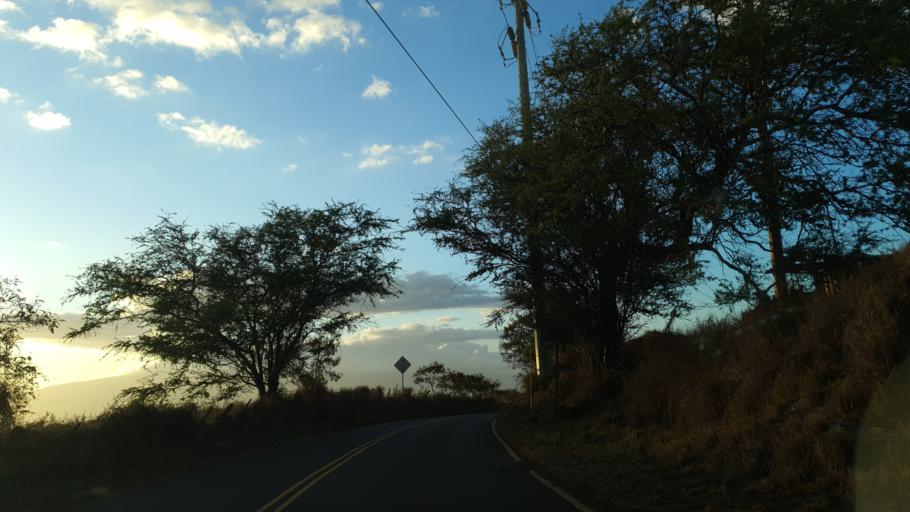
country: US
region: Hawaii
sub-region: Maui County
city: Pukalani
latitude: 20.7867
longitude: -156.3504
